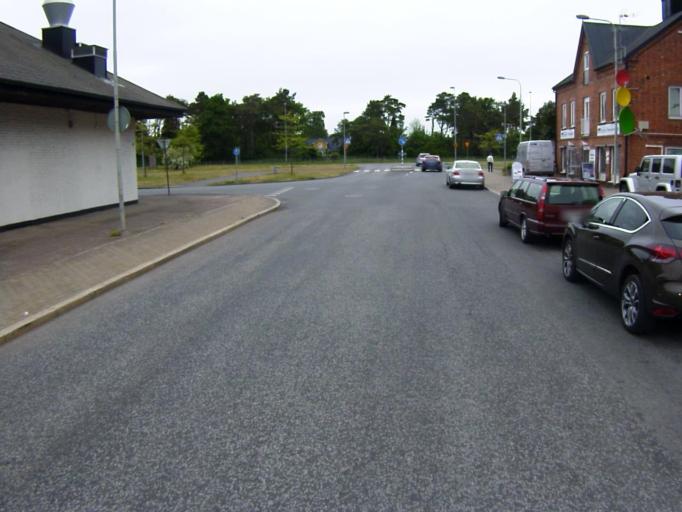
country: SE
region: Skane
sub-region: Kristianstads Kommun
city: Ahus
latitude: 55.9264
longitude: 14.3018
